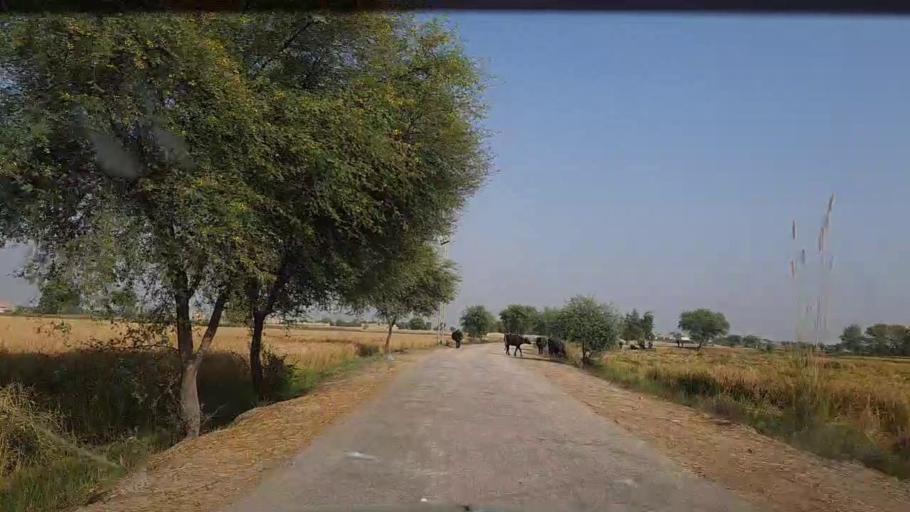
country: PK
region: Sindh
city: Shikarpur
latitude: 28.1169
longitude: 68.5744
